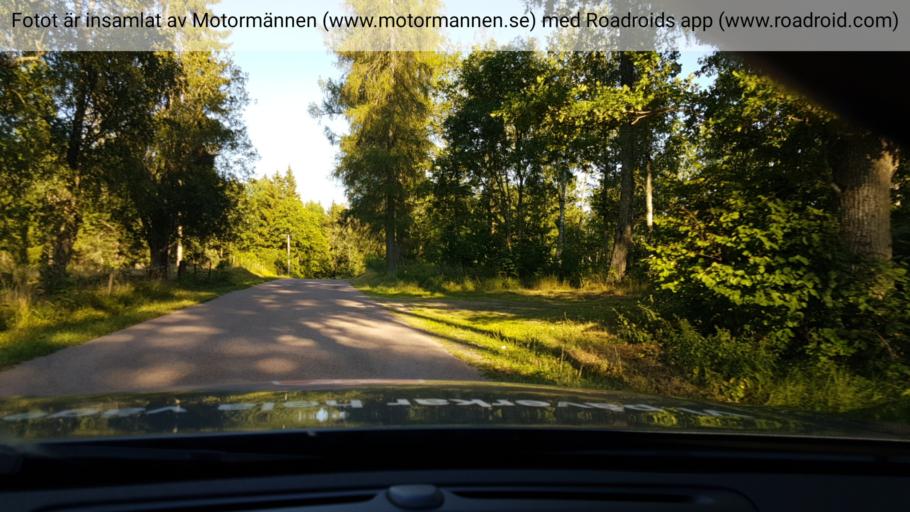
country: SE
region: Vaestmanland
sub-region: Surahammars Kommun
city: Ramnas
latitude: 59.6939
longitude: 16.0775
